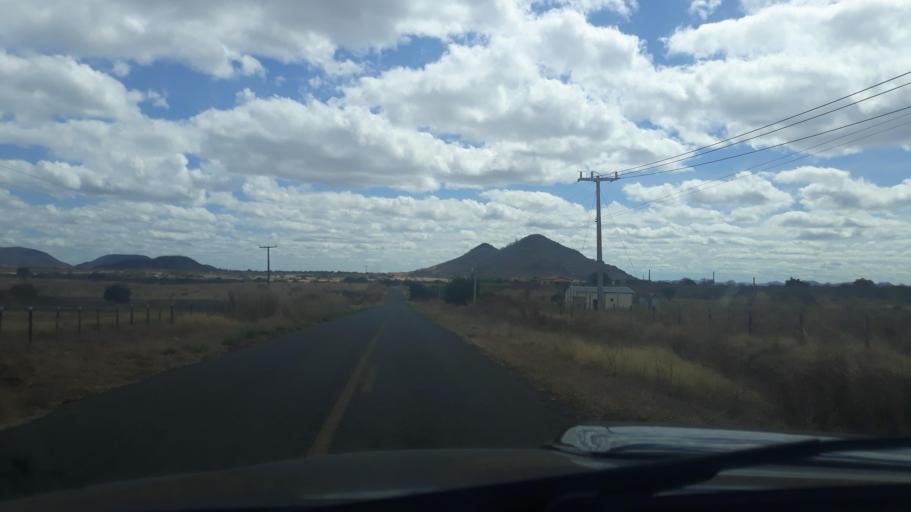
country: BR
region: Bahia
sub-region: Guanambi
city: Guanambi
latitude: -14.0833
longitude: -42.8764
